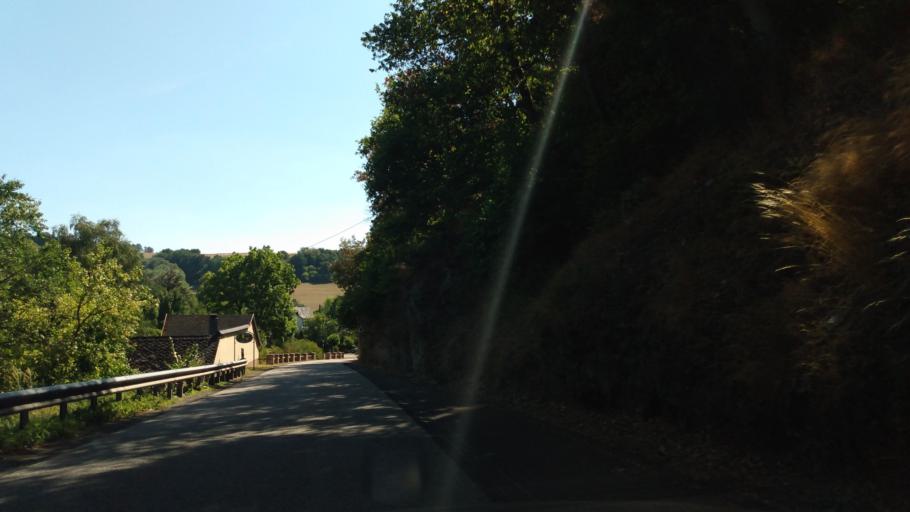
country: DE
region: Rheinland-Pfalz
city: Malborn
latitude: 49.7278
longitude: 6.9835
